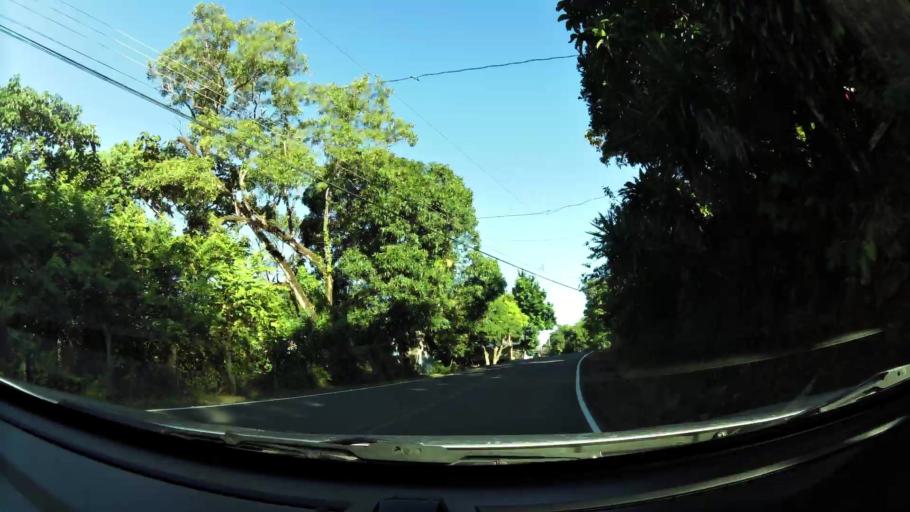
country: CR
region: Guanacaste
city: Juntas
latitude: 10.2048
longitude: -84.8471
